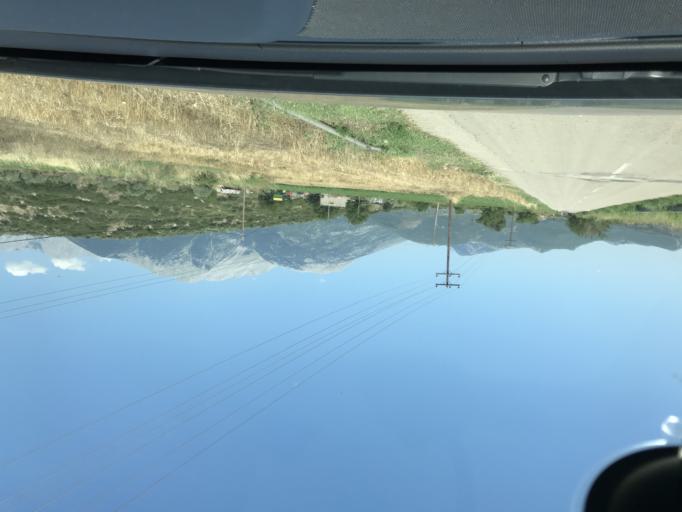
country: GR
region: Central Greece
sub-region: Nomos Fthiotidos
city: Elateia
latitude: 38.5272
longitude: 22.7972
